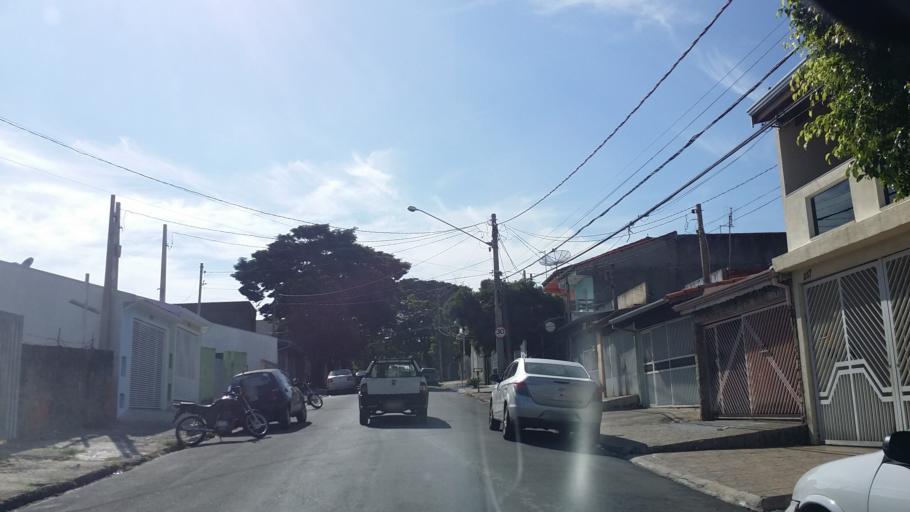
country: BR
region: Sao Paulo
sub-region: Indaiatuba
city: Indaiatuba
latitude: -23.1232
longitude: -47.2282
